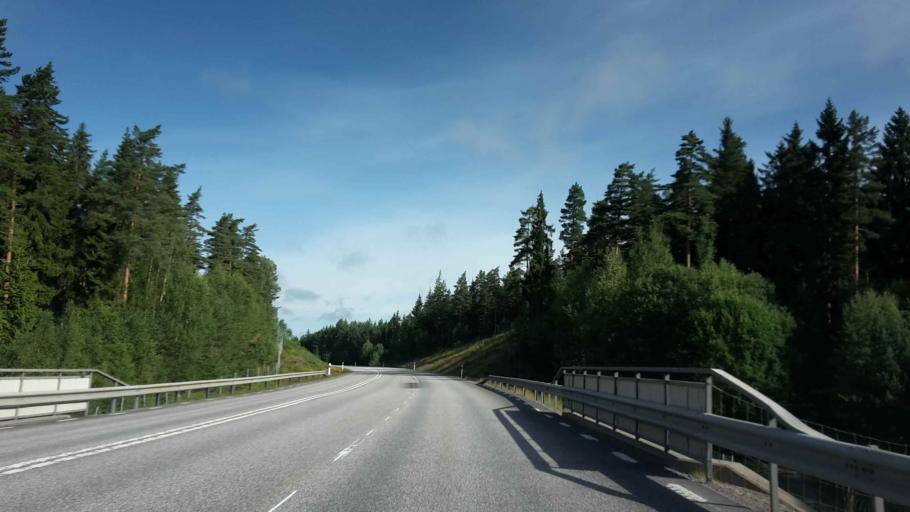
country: SE
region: OEstergoetland
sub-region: Motala Kommun
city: Borensberg
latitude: 58.5681
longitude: 15.3022
